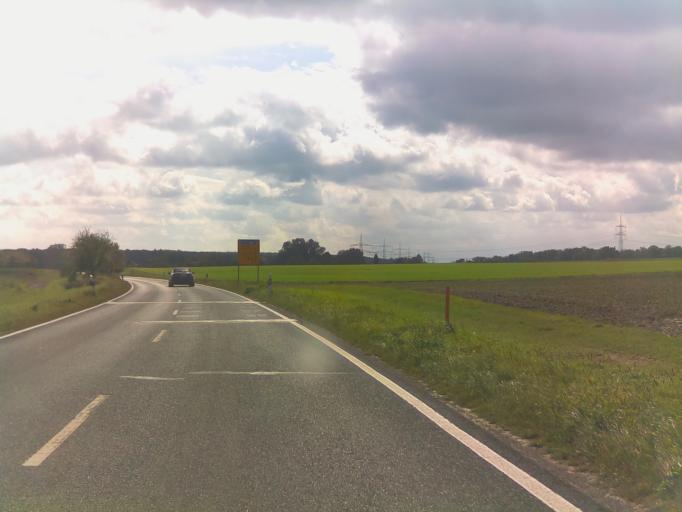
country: DE
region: Bavaria
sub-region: Regierungsbezirk Unterfranken
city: Frickenhausen
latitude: 49.7144
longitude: 10.0808
